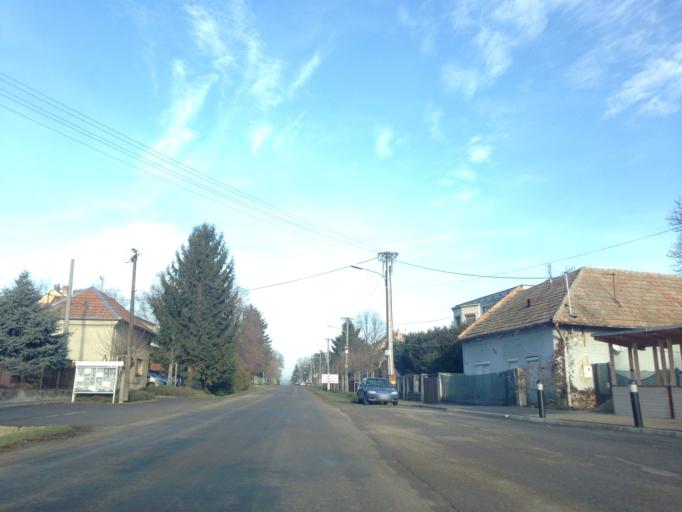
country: SK
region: Nitriansky
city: Svodin
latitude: 47.9575
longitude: 18.4120
